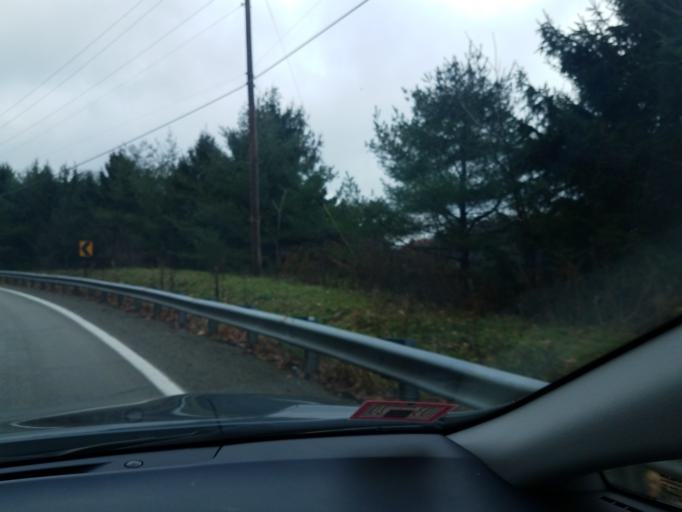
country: US
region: Pennsylvania
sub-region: Allegheny County
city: Franklin Park
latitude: 40.5643
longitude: -80.0609
